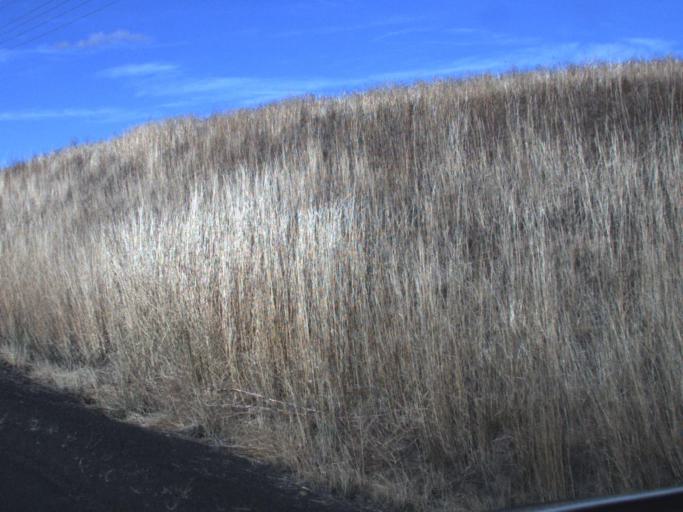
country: US
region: Washington
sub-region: Lincoln County
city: Davenport
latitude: 47.8333
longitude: -118.2112
